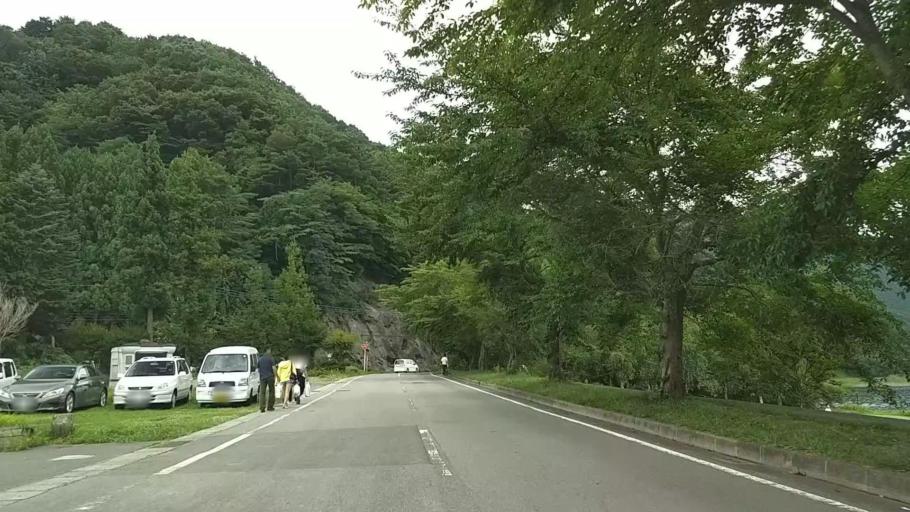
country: JP
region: Yamanashi
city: Fujikawaguchiko
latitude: 35.5043
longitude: 138.7338
